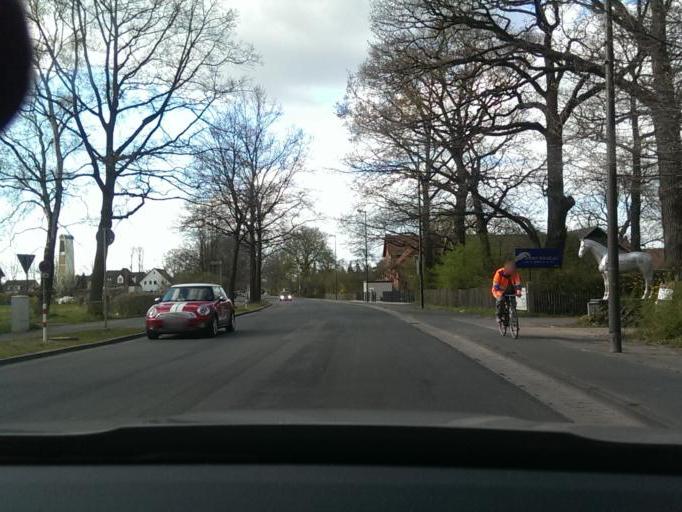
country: DE
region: Lower Saxony
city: Langenhagen
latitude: 52.4655
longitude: 9.7373
